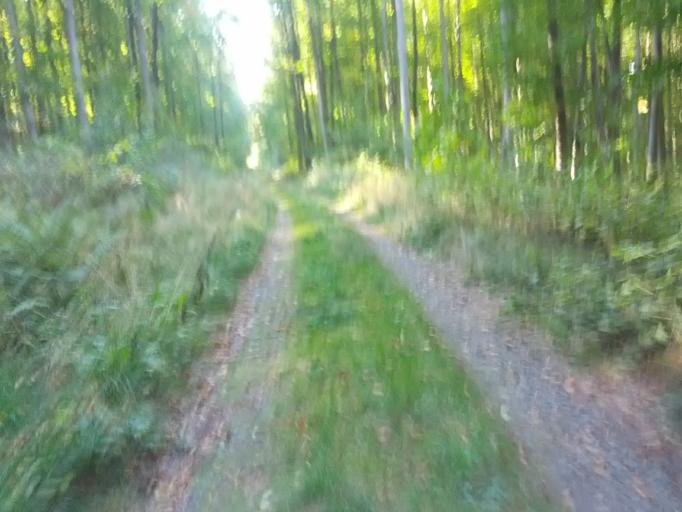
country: DE
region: Thuringia
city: Krauthausen
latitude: 51.0097
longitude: 10.2959
